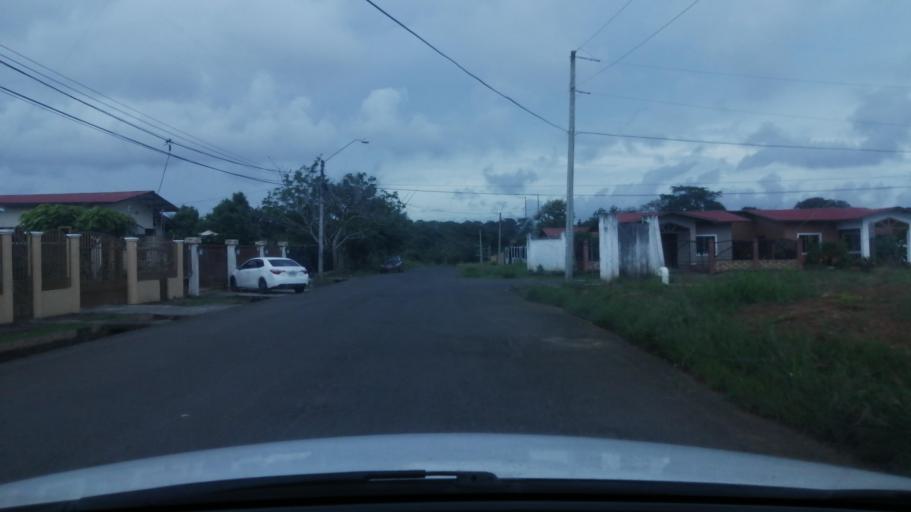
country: PA
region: Chiriqui
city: David
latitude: 8.4029
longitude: -82.4474
